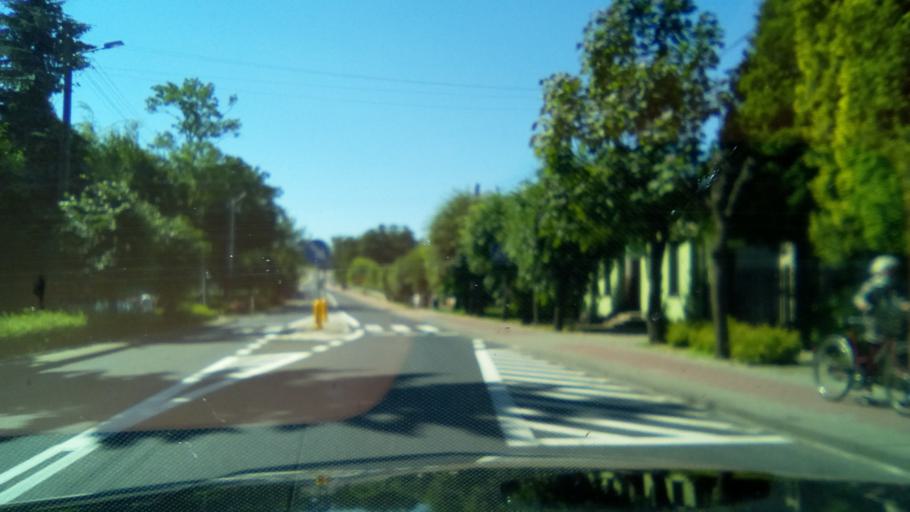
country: PL
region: Lodz Voivodeship
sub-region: Powiat tomaszowski
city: Inowlodz
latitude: 51.5225
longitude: 20.2231
